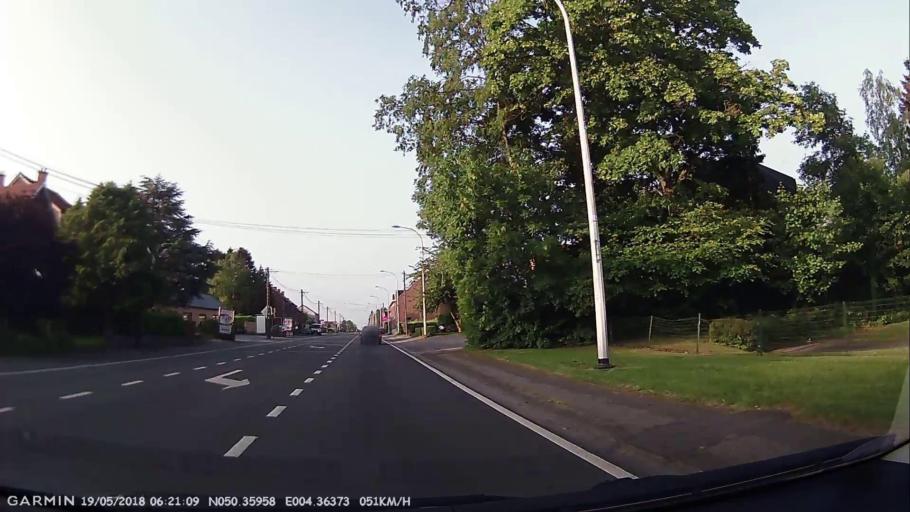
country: BE
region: Wallonia
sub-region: Province du Hainaut
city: Thuin
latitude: 50.3595
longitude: 4.3637
